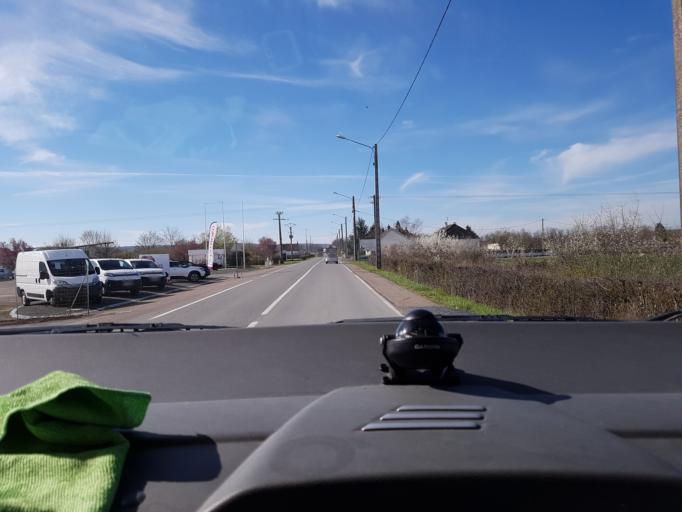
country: FR
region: Bourgogne
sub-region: Departement de Saone-et-Loire
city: Gueugnon
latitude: 46.5898
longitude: 4.0649
